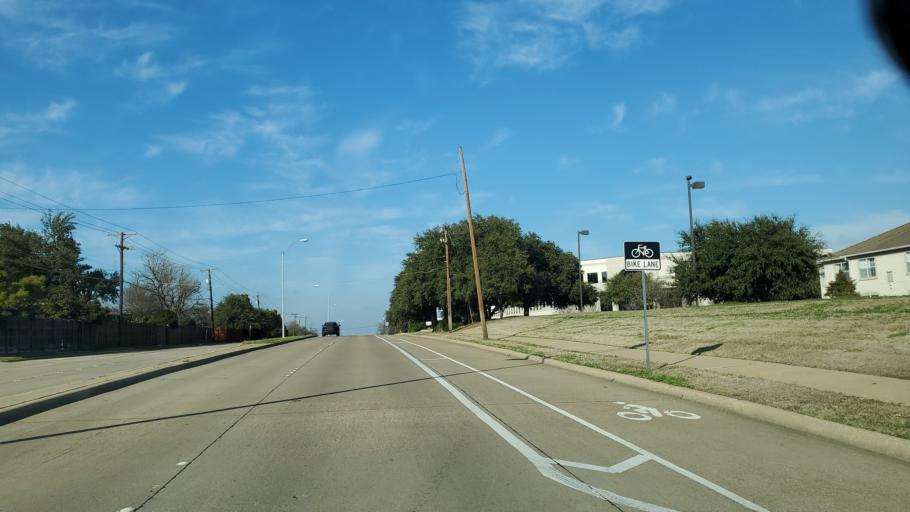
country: US
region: Texas
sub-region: Dallas County
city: Richardson
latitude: 32.9806
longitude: -96.7170
